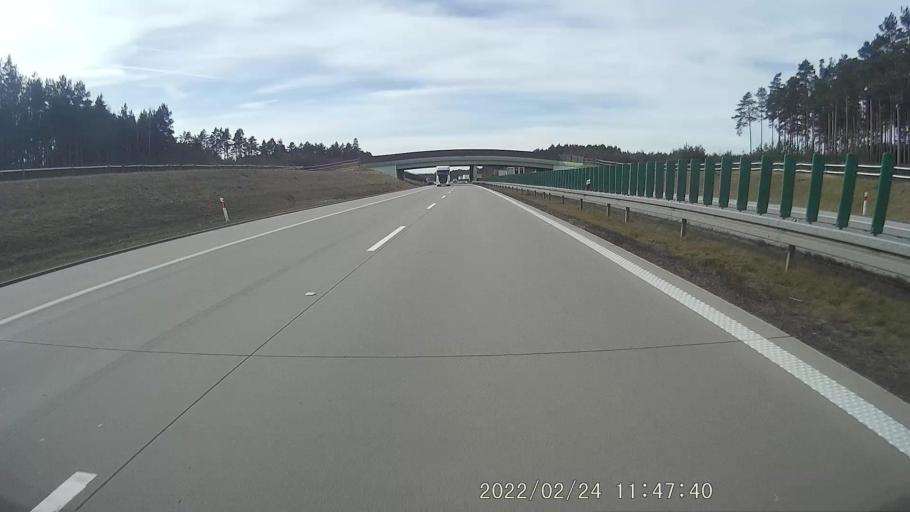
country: PL
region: Lower Silesian Voivodeship
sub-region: Powiat polkowicki
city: Radwanice
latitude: 51.5773
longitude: 15.9519
